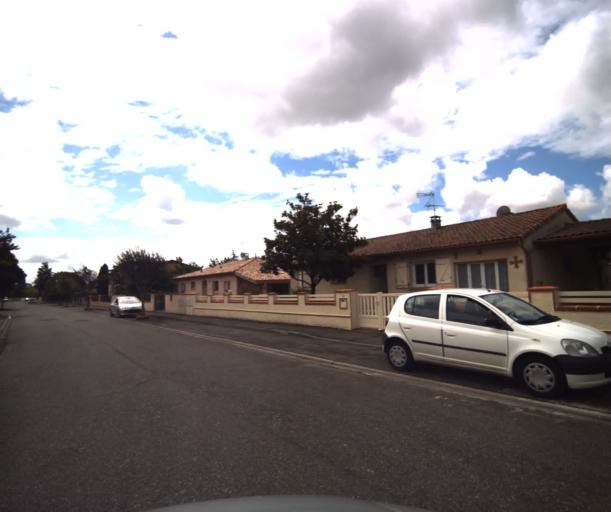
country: FR
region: Midi-Pyrenees
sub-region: Departement de la Haute-Garonne
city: Pinsaguel
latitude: 43.5177
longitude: 1.3897
